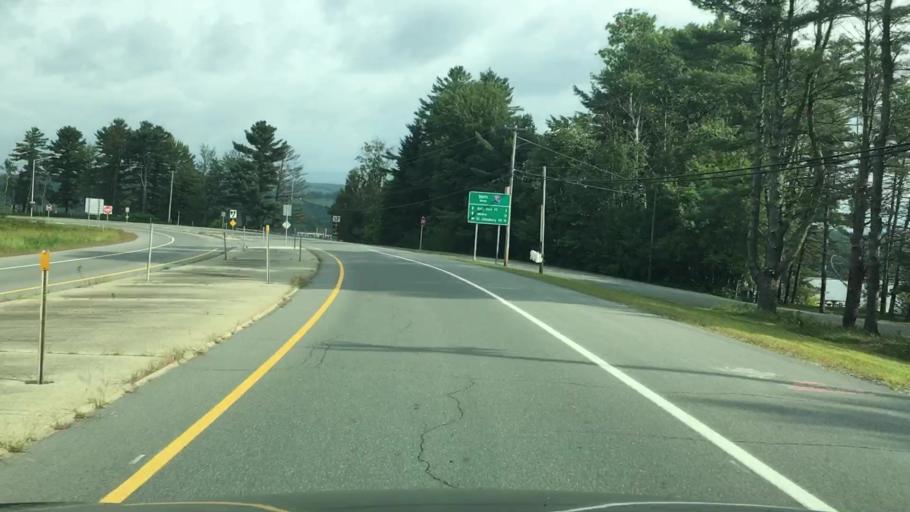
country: US
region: New Hampshire
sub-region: Grafton County
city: Littleton
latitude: 44.3314
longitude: -71.8740
